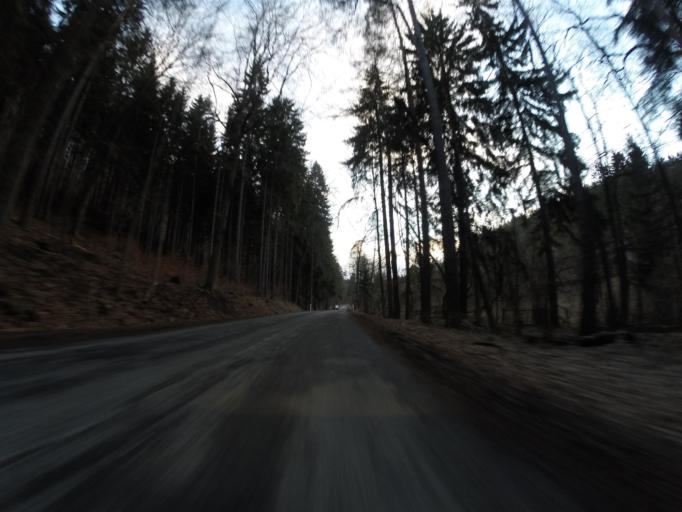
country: DE
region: Thuringia
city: Bucha
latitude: 50.9301
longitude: 11.5365
